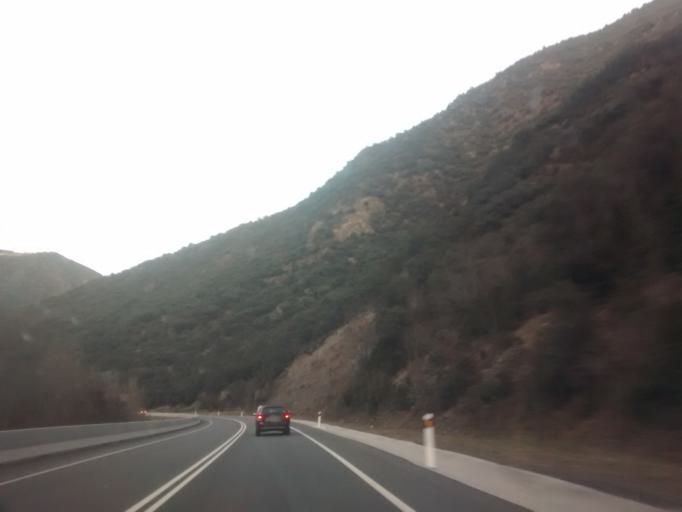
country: AD
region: Sant Julia de Loria
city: Sant Julia de Loria
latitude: 42.4154
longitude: 1.4646
